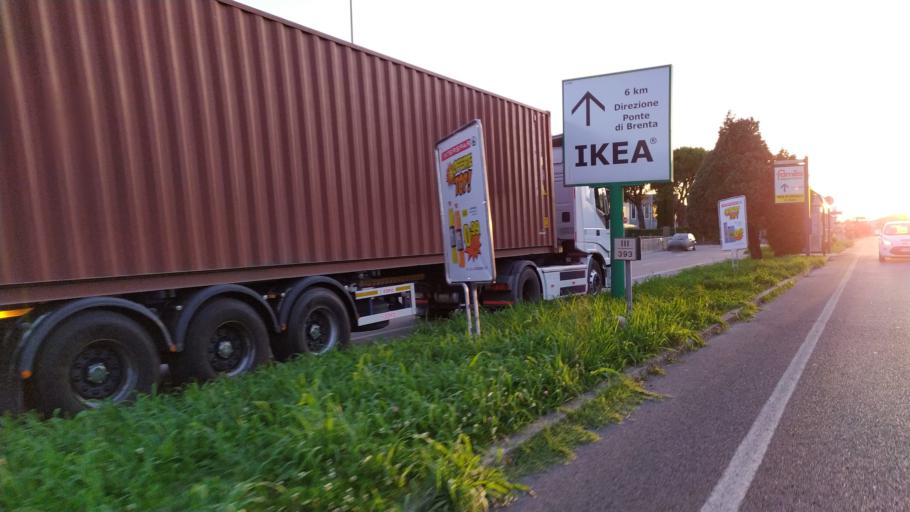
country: IT
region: Veneto
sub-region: Provincia di Padova
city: Vigonza
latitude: 45.4218
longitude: 11.9791
